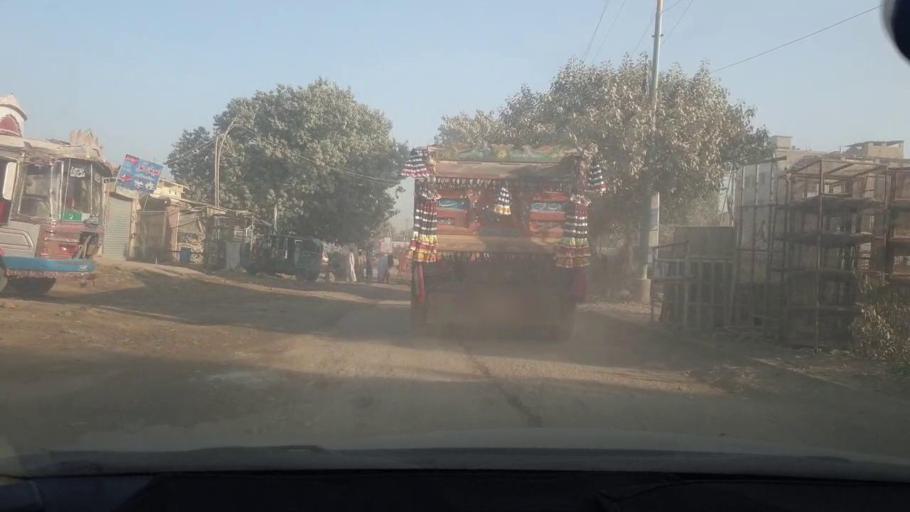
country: PK
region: Sindh
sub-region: Karachi District
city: Karachi
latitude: 24.9743
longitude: 67.0400
